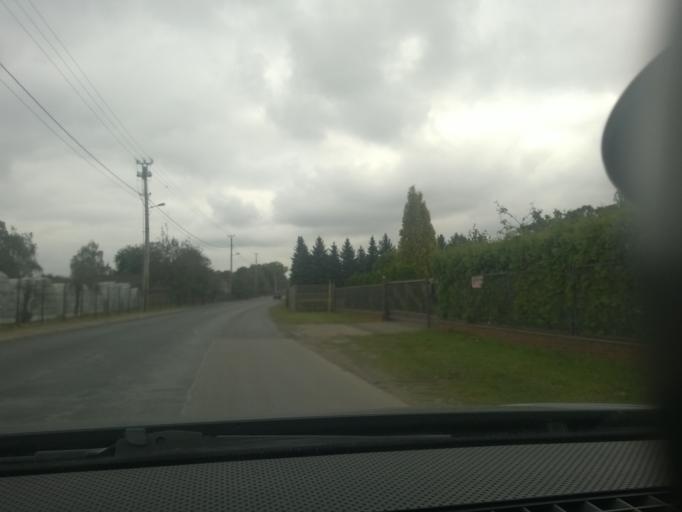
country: PL
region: Greater Poland Voivodeship
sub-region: Kalisz
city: Kalisz
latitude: 51.7264
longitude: 18.1382
